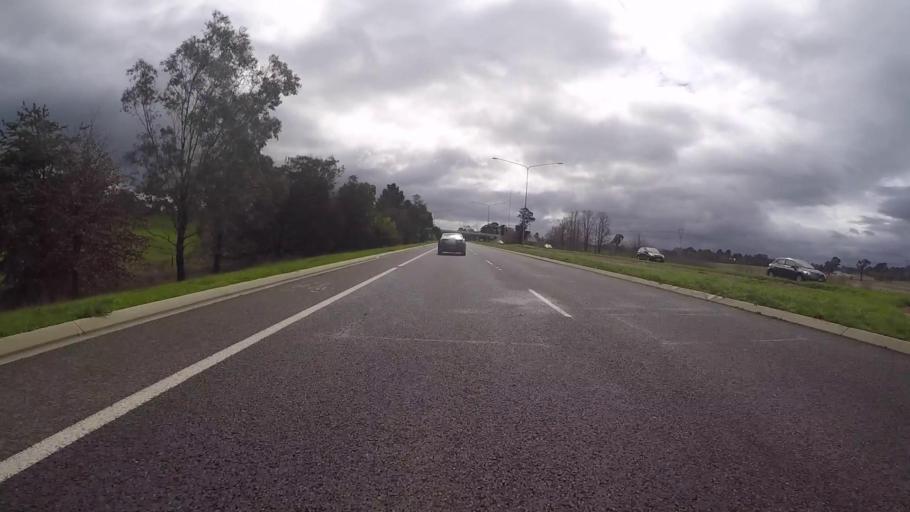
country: AU
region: Australian Capital Territory
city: Kaleen
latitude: -35.2291
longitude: 149.1237
